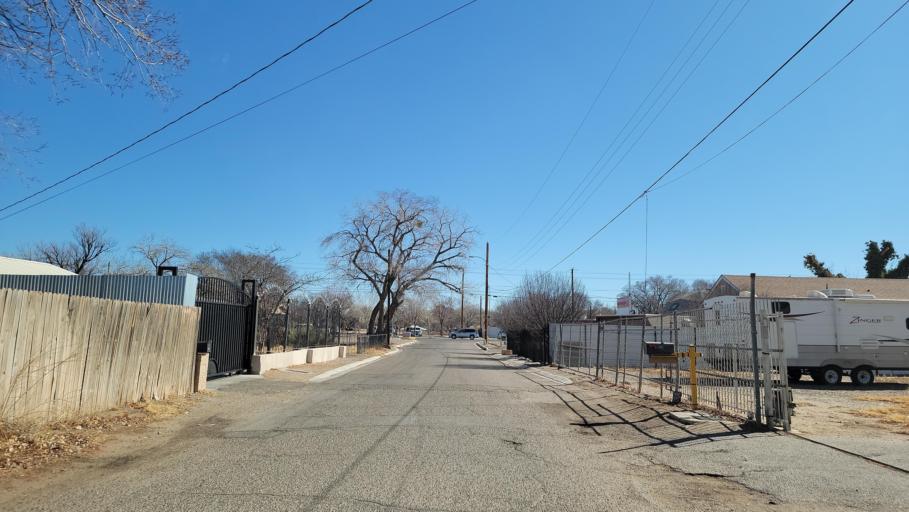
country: US
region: New Mexico
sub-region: Bernalillo County
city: South Valley
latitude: 35.0323
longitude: -106.6806
